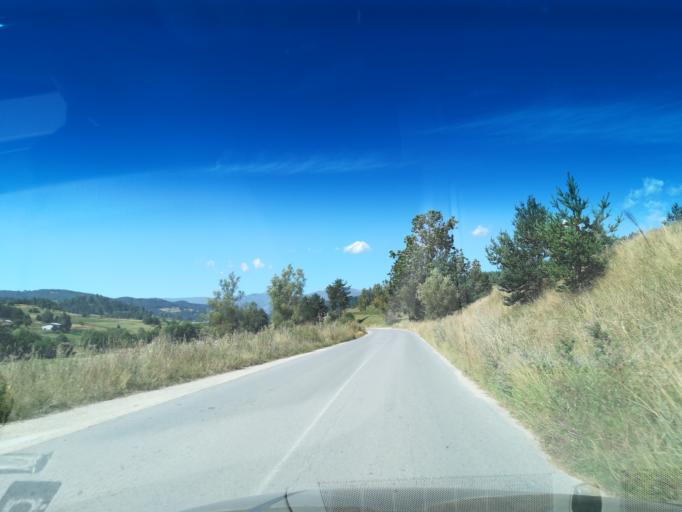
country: BG
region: Sofiya
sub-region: Obshtina Koprivshtitsa
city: Koprivshtitsa
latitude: 42.6089
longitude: 24.3766
